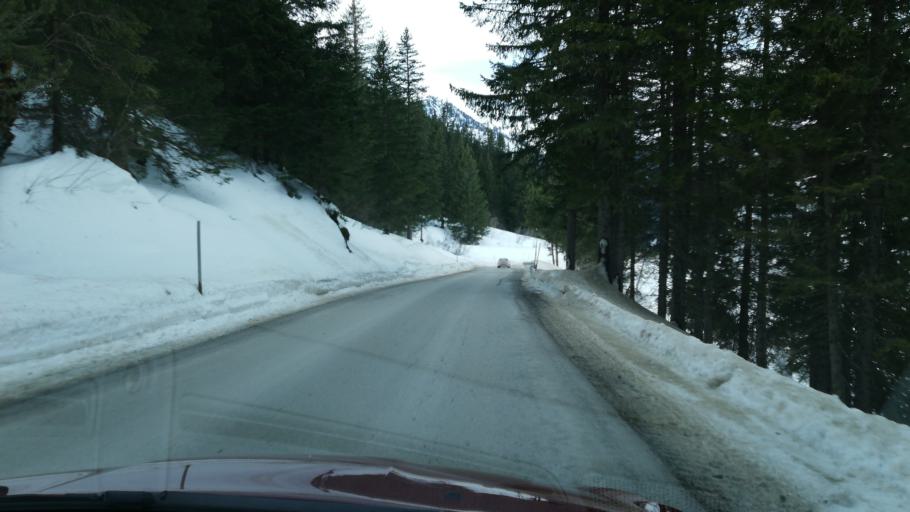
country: AT
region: Styria
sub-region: Politischer Bezirk Liezen
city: Donnersbach
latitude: 47.4073
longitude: 14.1927
